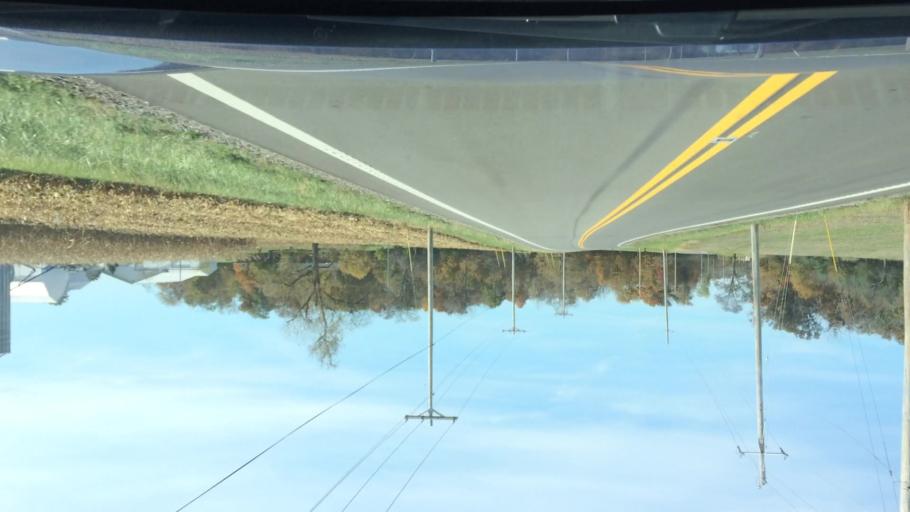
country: US
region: Ohio
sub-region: Logan County
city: Russells Point
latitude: 40.4394
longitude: -83.8754
